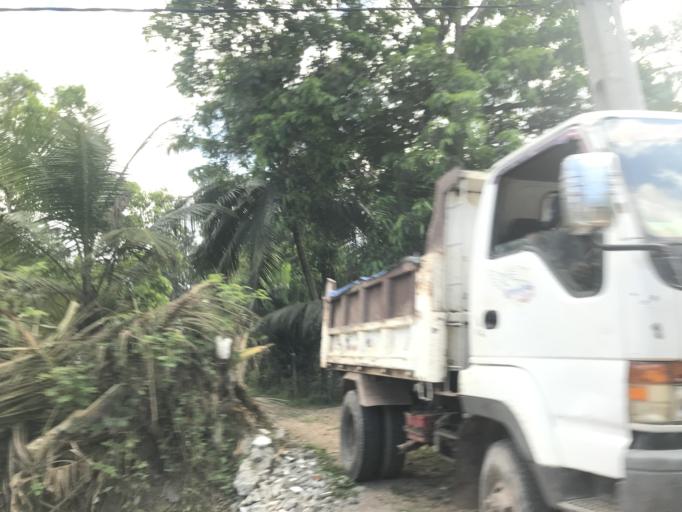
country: LK
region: Western
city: Gampaha
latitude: 7.0739
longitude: 79.9925
